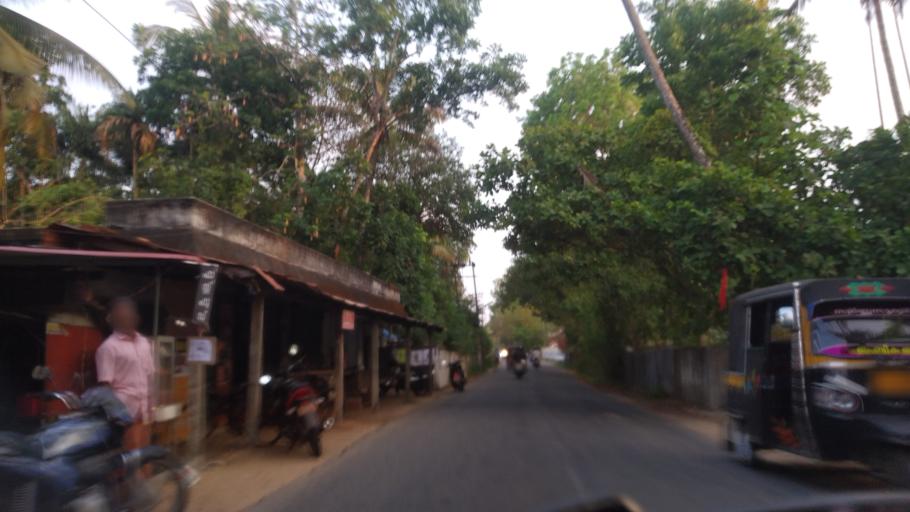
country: IN
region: Kerala
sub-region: Thrissur District
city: Kodungallur
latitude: 10.2609
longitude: 76.1445
